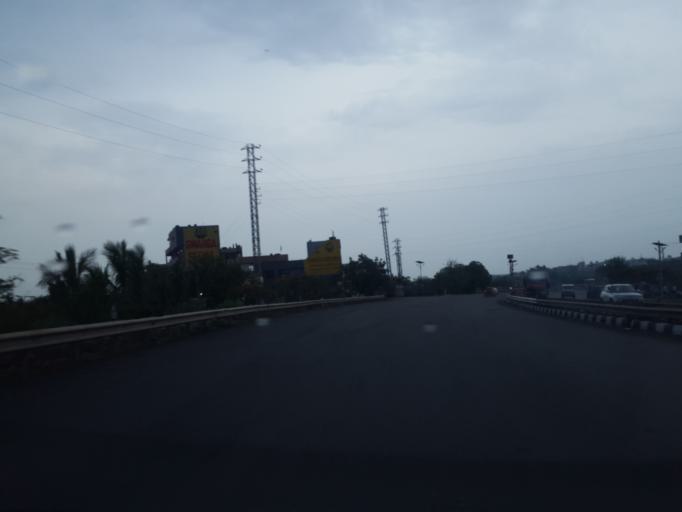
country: IN
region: Telangana
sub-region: Mahbubnagar
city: Farrukhnagar
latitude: 17.1454
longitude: 78.2921
